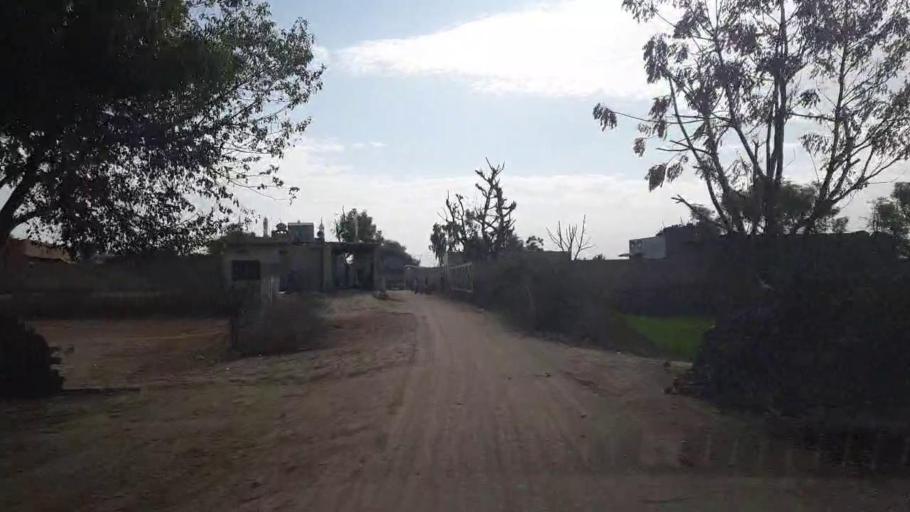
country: PK
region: Sindh
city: Sakrand
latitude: 25.9890
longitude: 68.3406
